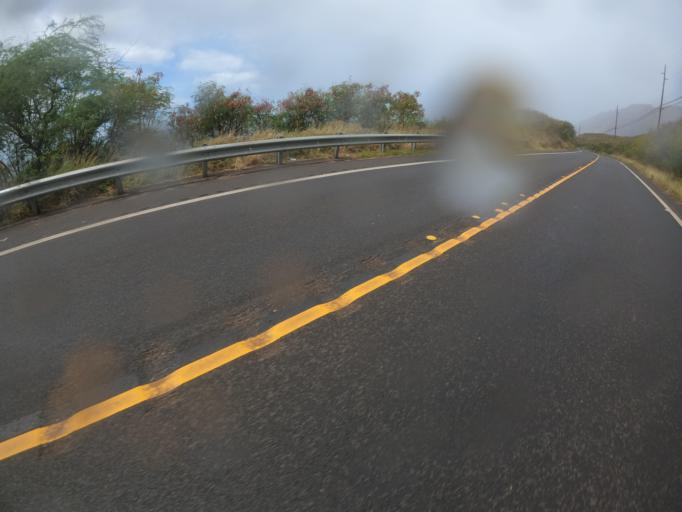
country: US
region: Hawaii
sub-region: Honolulu County
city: Makaha Valley
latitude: 21.5436
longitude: -158.2379
